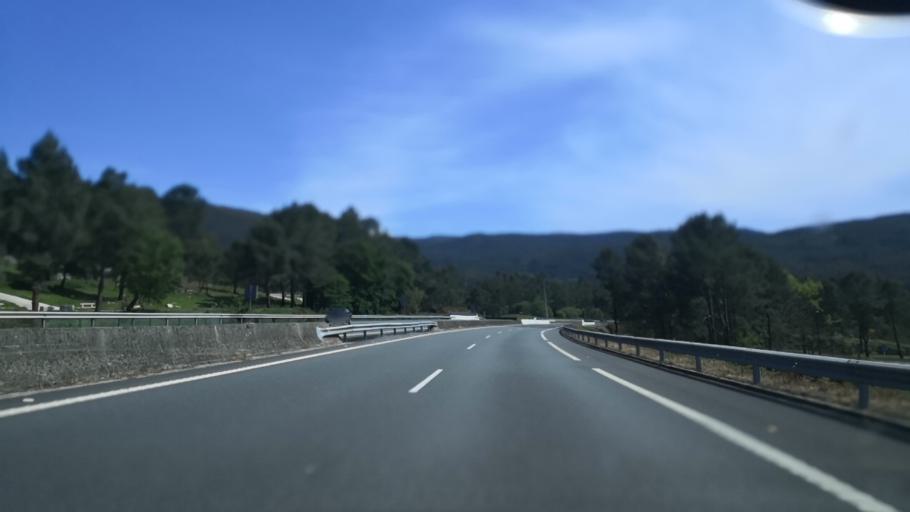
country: ES
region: Galicia
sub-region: Provincia da Coruna
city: Padron
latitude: 42.7355
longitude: -8.6396
